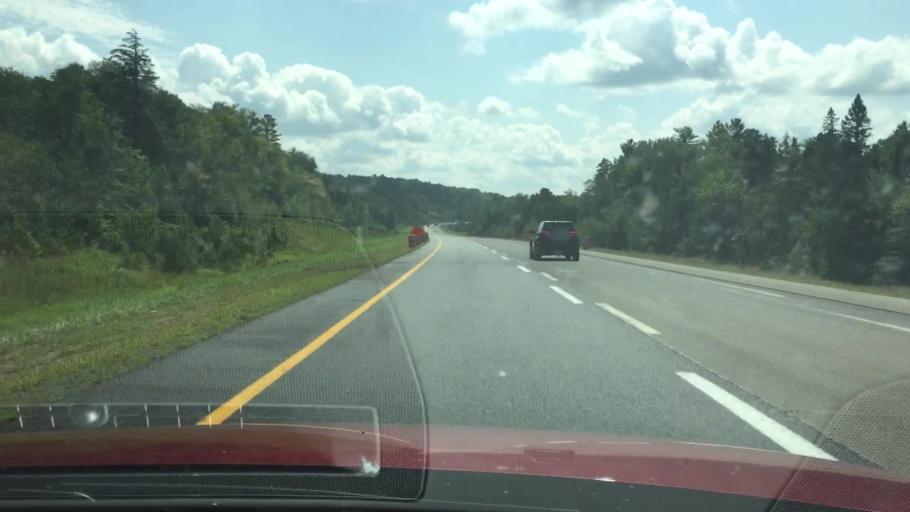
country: US
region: Maine
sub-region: Penobscot County
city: Medway
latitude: 45.7188
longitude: -68.4755
